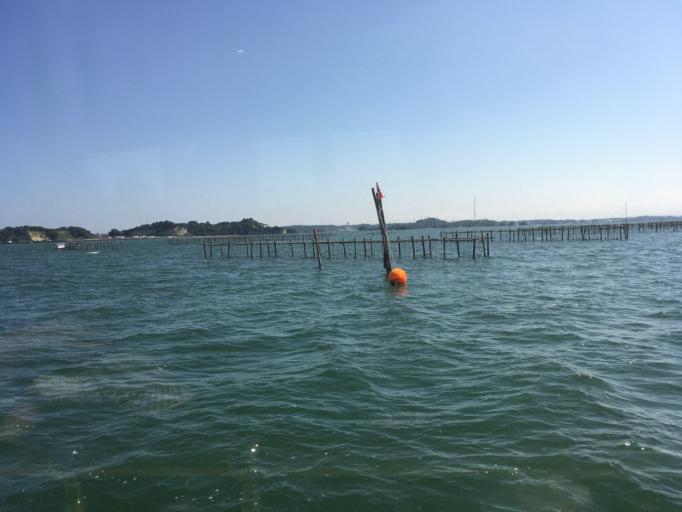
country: JP
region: Miyagi
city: Matsushima
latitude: 38.3505
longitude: 141.0901
